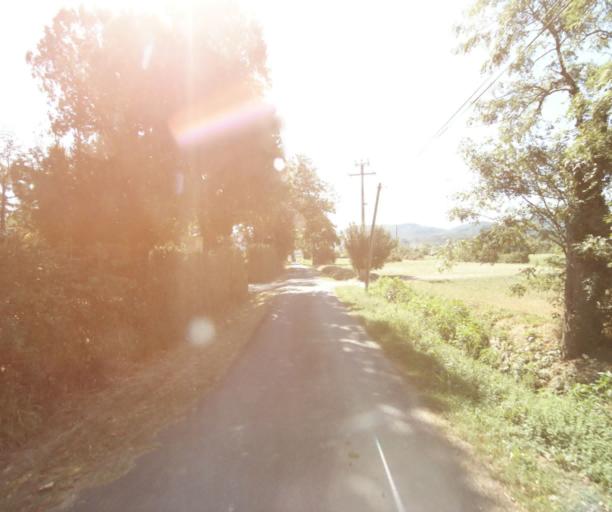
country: FR
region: Midi-Pyrenees
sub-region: Departement de la Haute-Garonne
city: Revel
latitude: 43.4586
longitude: 2.0310
